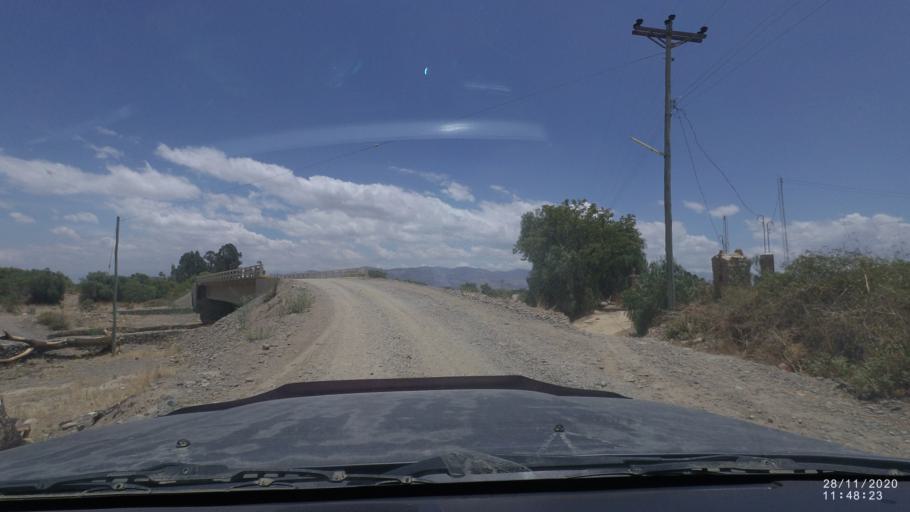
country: BO
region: Cochabamba
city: Tarata
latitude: -17.6392
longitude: -66.0325
